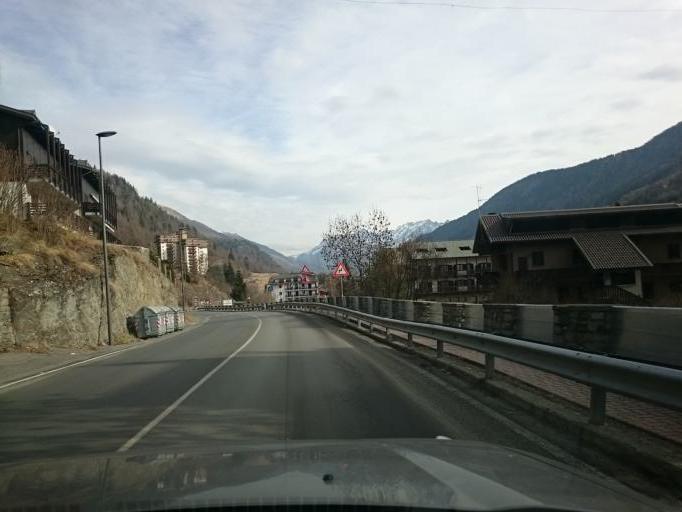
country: IT
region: Lombardy
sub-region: Provincia di Sondrio
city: Aprica
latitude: 46.1563
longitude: 10.1637
